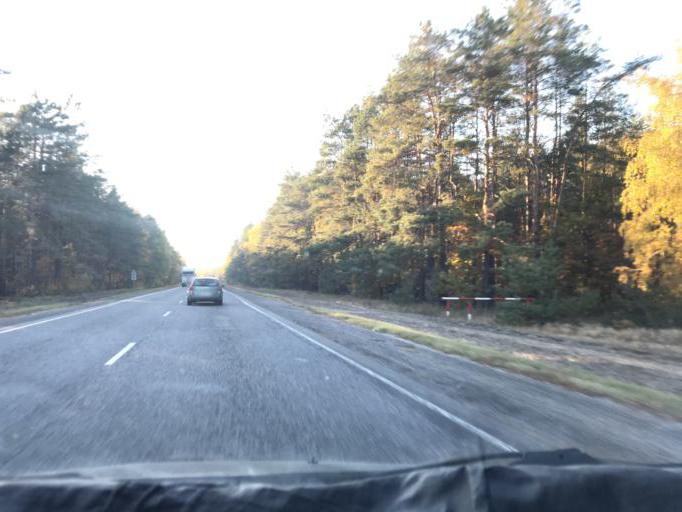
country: BY
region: Gomel
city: Zhytkavichy
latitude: 52.2727
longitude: 28.0161
